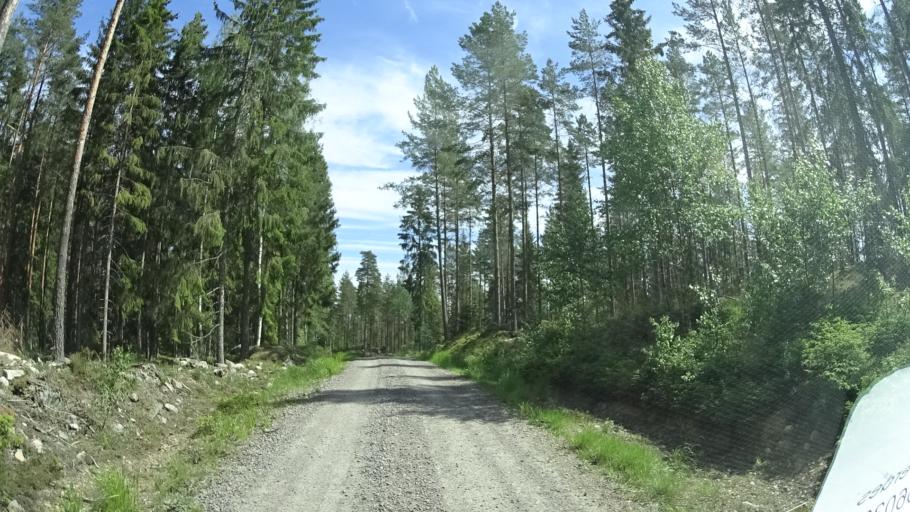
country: SE
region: OEstergoetland
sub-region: Norrkopings Kommun
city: Svartinge
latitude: 58.7809
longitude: 15.9186
